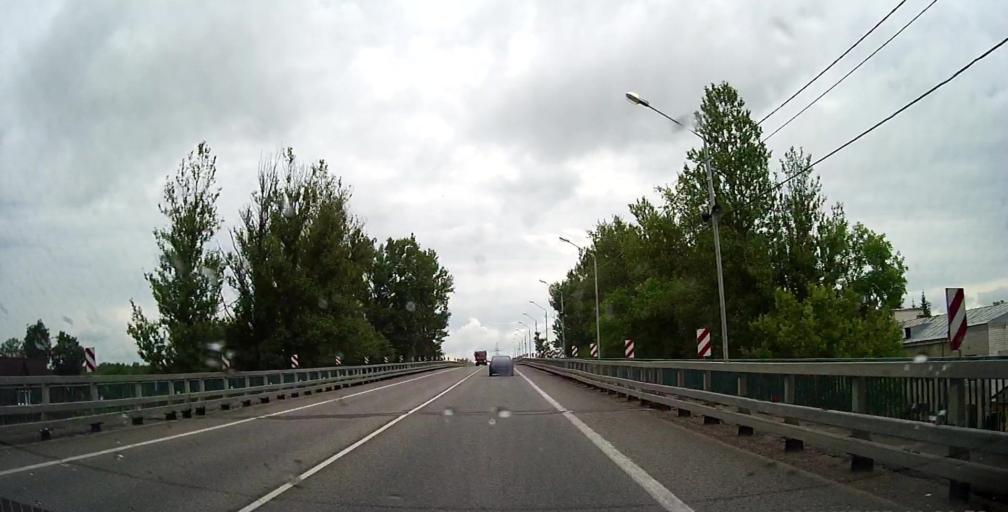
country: RU
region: Smolensk
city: Katyn'
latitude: 54.7824
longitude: 31.8206
